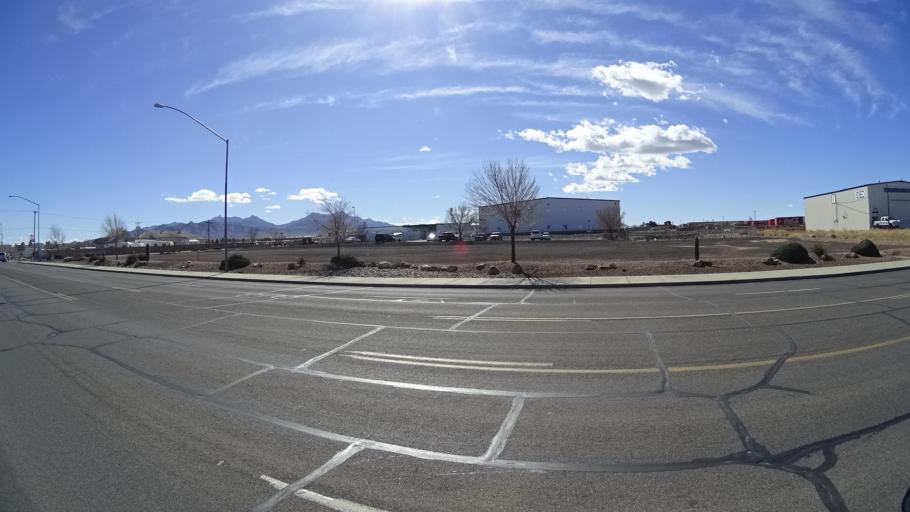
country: US
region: Arizona
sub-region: Mohave County
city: New Kingman-Butler
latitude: 35.2250
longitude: -114.0192
